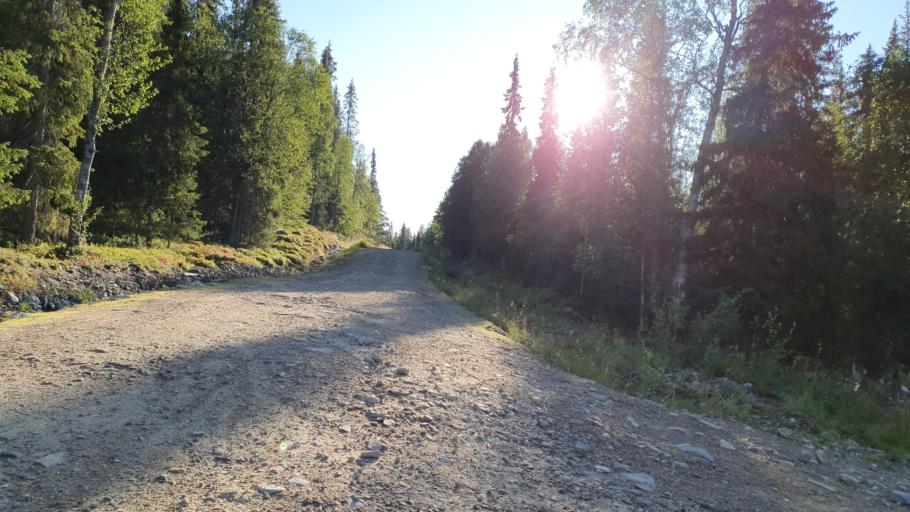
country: FI
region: Lapland
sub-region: Tunturi-Lappi
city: Kolari
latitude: 67.5985
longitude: 24.2033
